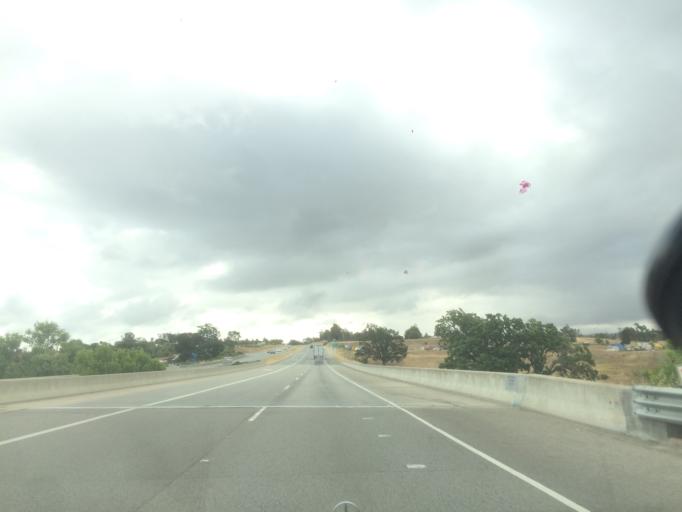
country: US
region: California
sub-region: San Luis Obispo County
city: Paso Robles
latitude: 35.6444
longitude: -120.6467
